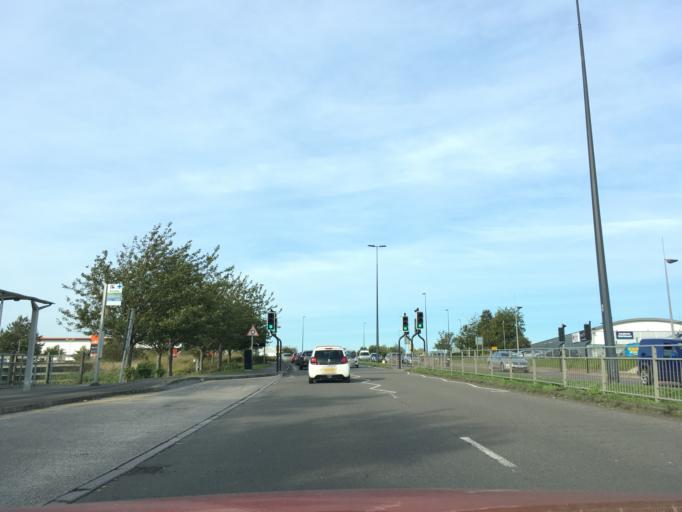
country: GB
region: England
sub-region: South Gloucestershire
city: Almondsbury
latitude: 51.5262
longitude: -2.6033
